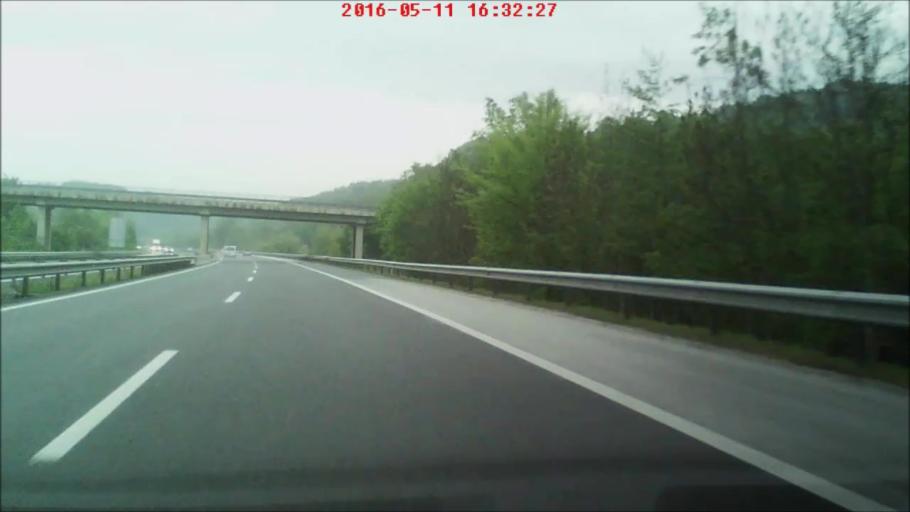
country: SI
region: Kungota
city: Zgornja Kungota
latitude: 46.6460
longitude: 15.6496
